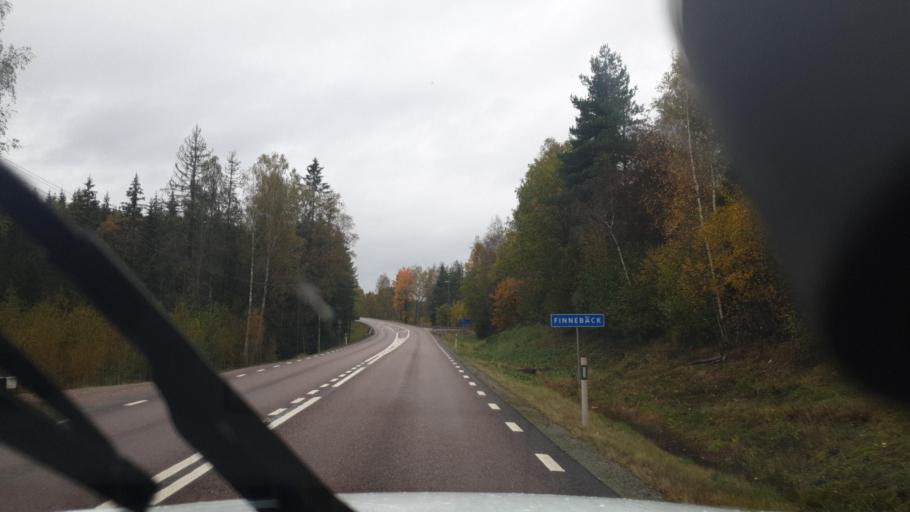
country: SE
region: Vaermland
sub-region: Sunne Kommun
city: Sunne
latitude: 59.6530
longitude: 12.9449
